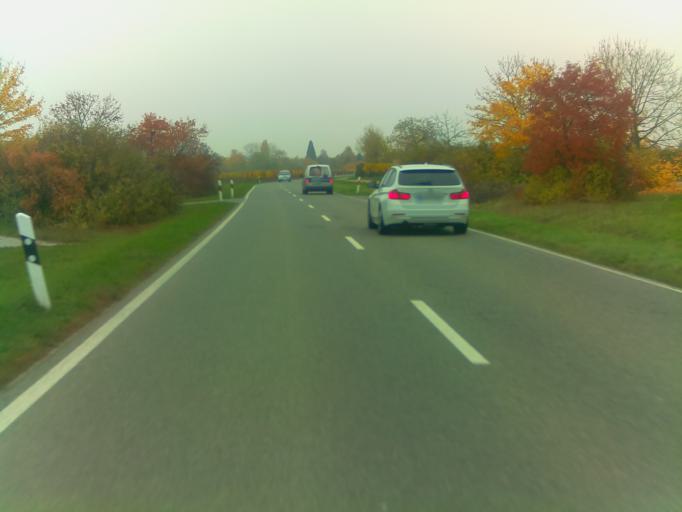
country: DE
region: Rheinland-Pfalz
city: Friedelsheim
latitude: 49.4453
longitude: 8.2060
